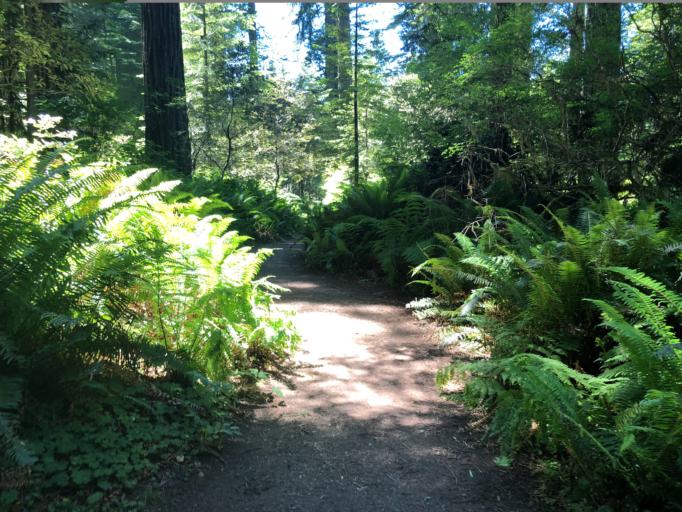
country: US
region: California
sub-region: Humboldt County
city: Westhaven-Moonstone
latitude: 41.3093
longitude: -124.0250
